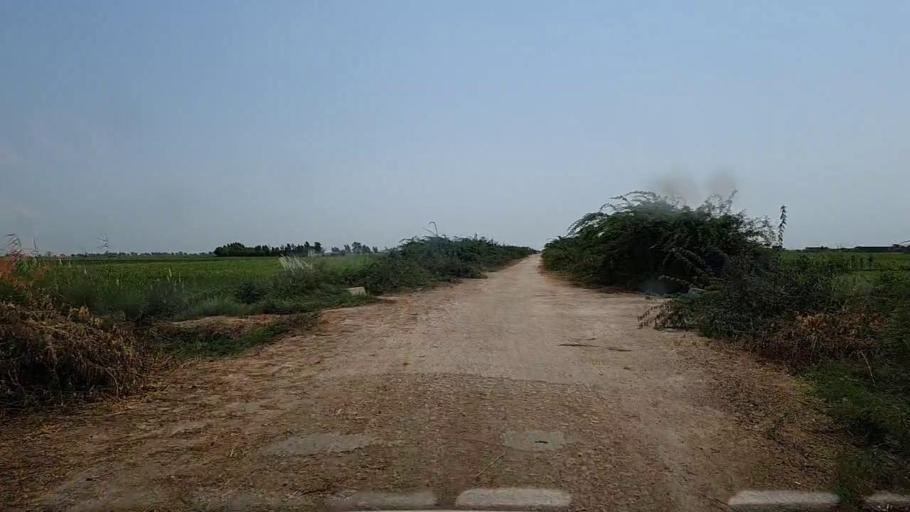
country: PK
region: Sindh
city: Mirpur Batoro
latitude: 24.6287
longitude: 68.4522
